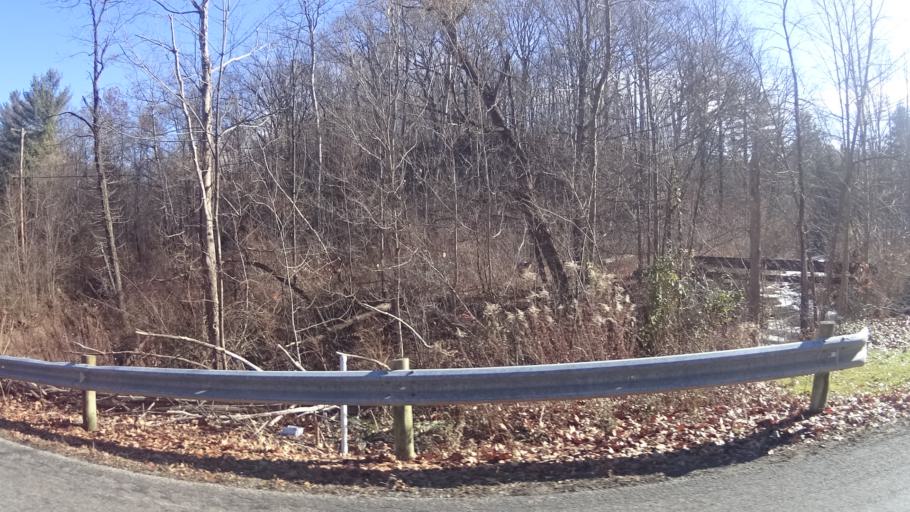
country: US
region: Ohio
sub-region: Lorain County
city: South Amherst
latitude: 41.3483
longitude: -82.2901
